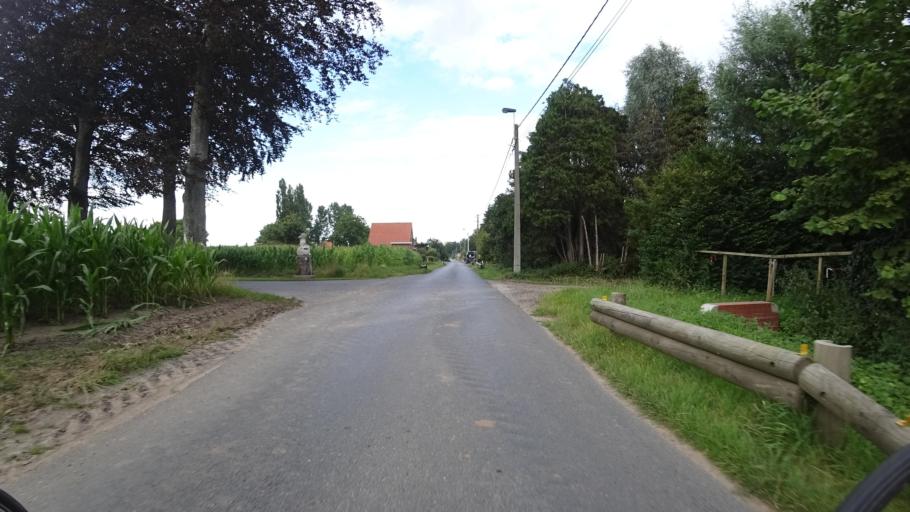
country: BE
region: Flanders
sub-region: Provincie West-Vlaanderen
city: Oostkamp
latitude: 51.1695
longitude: 3.2776
